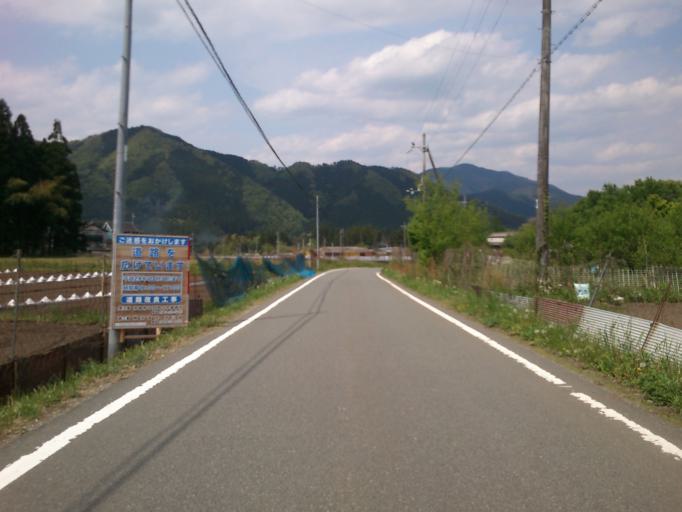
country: JP
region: Kyoto
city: Fukuchiyama
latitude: 35.3355
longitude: 134.9340
